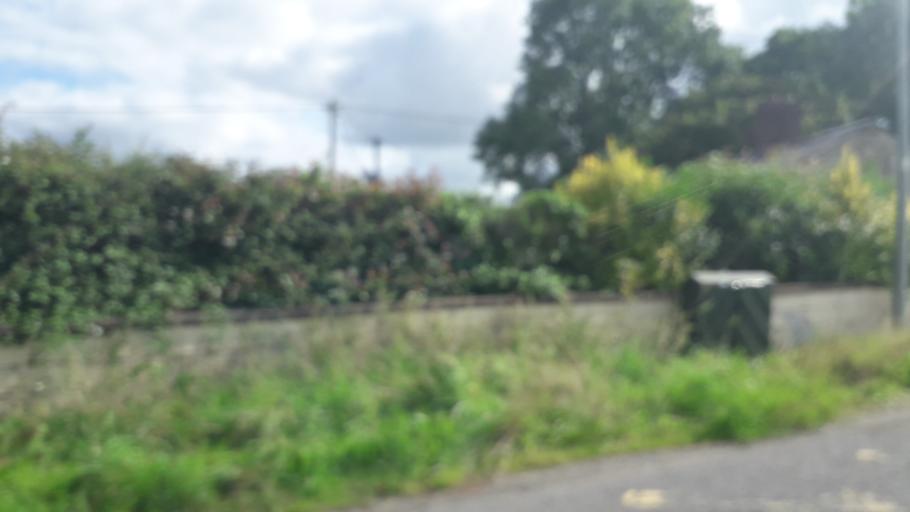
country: IE
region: Leinster
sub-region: Lu
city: Dundalk
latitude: 54.0442
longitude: -6.3657
